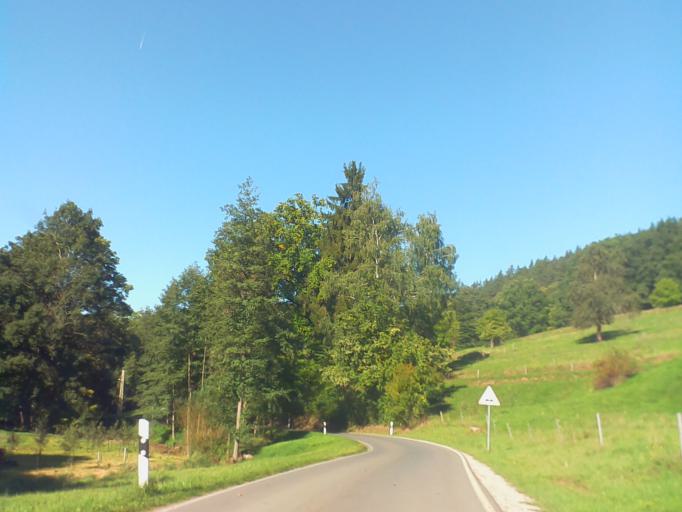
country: DE
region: Thuringia
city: Schwarzbach
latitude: 50.8061
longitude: 11.8553
